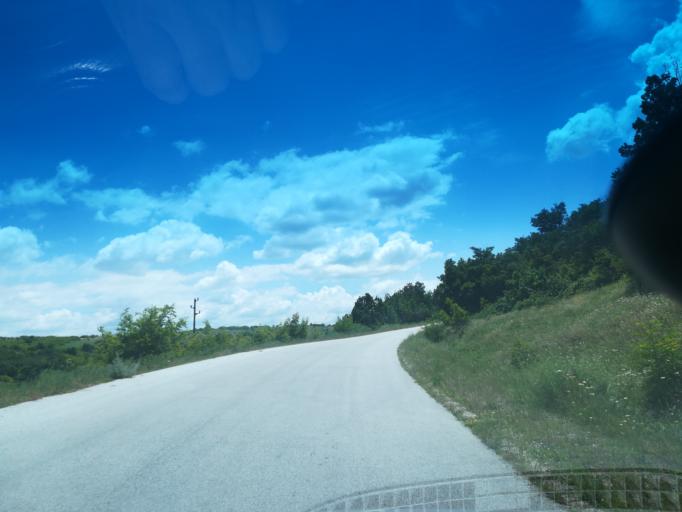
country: BG
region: Khaskovo
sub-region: Obshtina Mineralni Bani
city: Mineralni Bani
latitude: 41.9649
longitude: 25.2610
